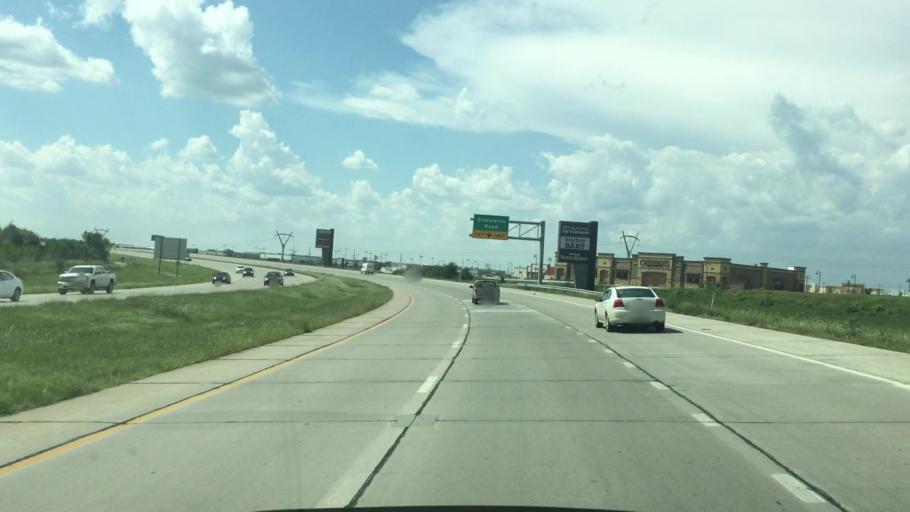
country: US
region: Kansas
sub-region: Butler County
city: Andover
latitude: 37.7281
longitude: -97.2010
